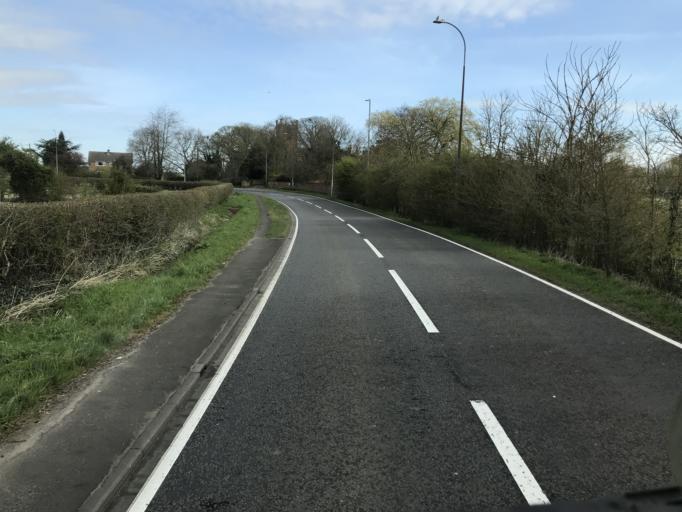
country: GB
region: England
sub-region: Lincolnshire
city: Market Rasen
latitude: 53.3882
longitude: -0.4007
